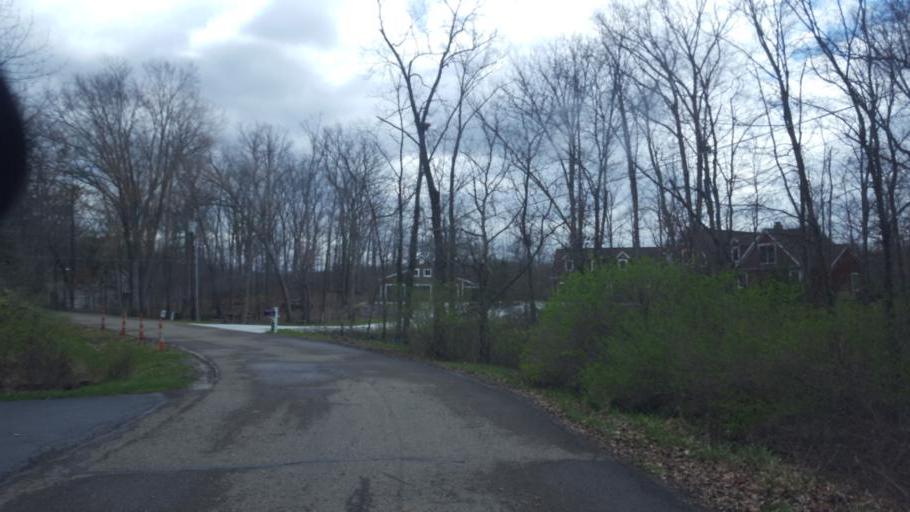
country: US
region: Ohio
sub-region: Franklin County
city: Westerville
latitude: 40.1257
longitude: -82.8732
